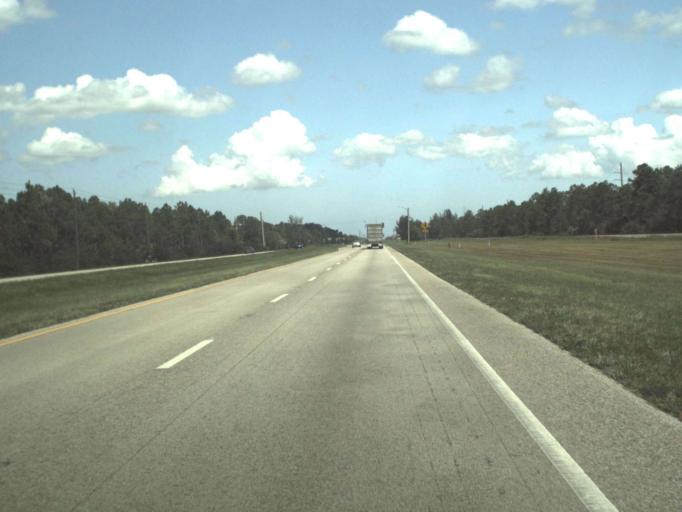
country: US
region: Florida
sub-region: Palm Beach County
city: Palm Beach Gardens
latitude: 26.8767
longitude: -80.2525
